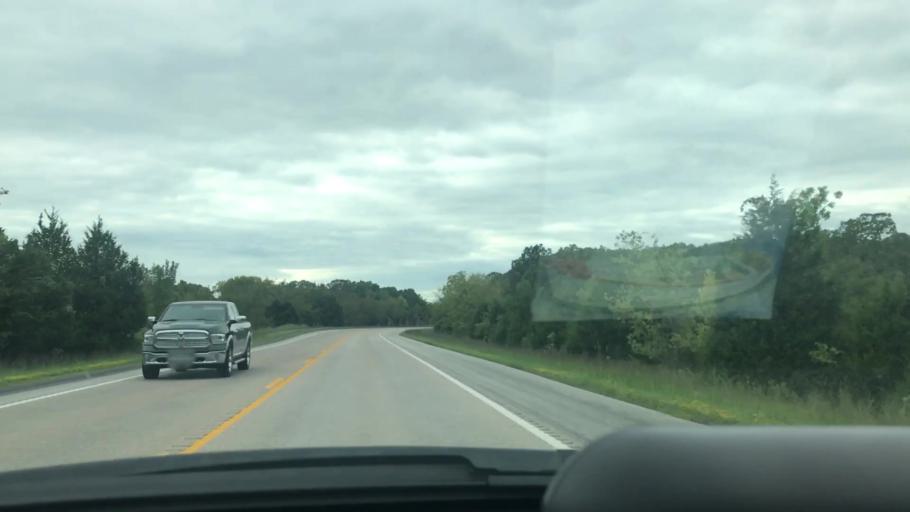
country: US
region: Missouri
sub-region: Benton County
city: Warsaw
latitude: 38.2114
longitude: -93.3410
